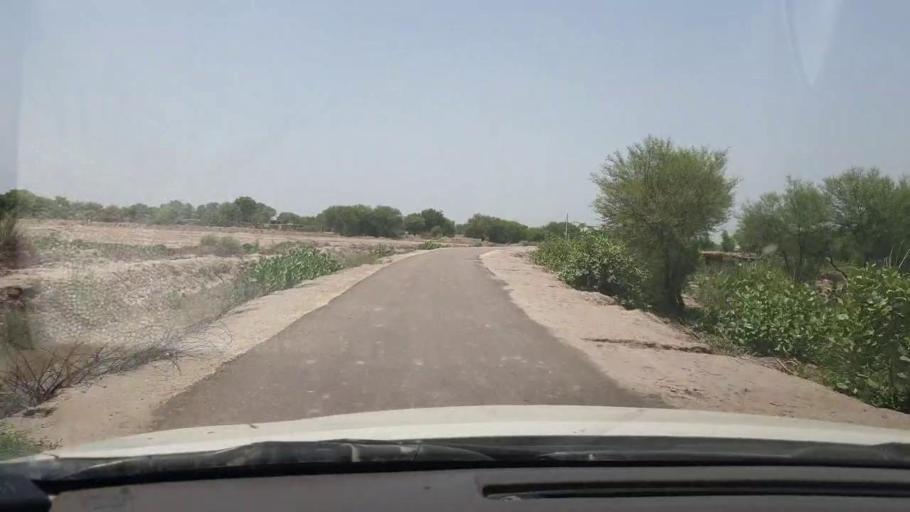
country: PK
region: Sindh
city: Rohri
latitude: 27.5163
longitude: 69.1807
